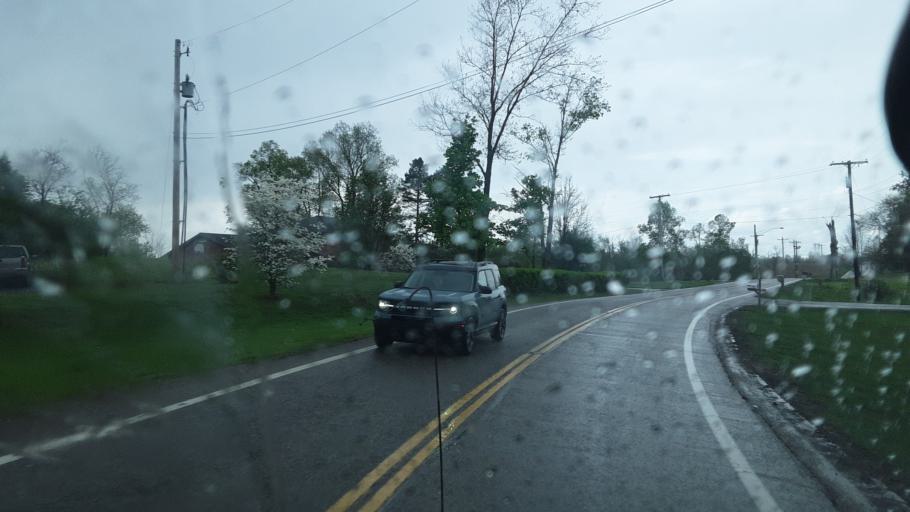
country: US
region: Ohio
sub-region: Muskingum County
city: New Concord
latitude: 40.0128
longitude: -81.7478
